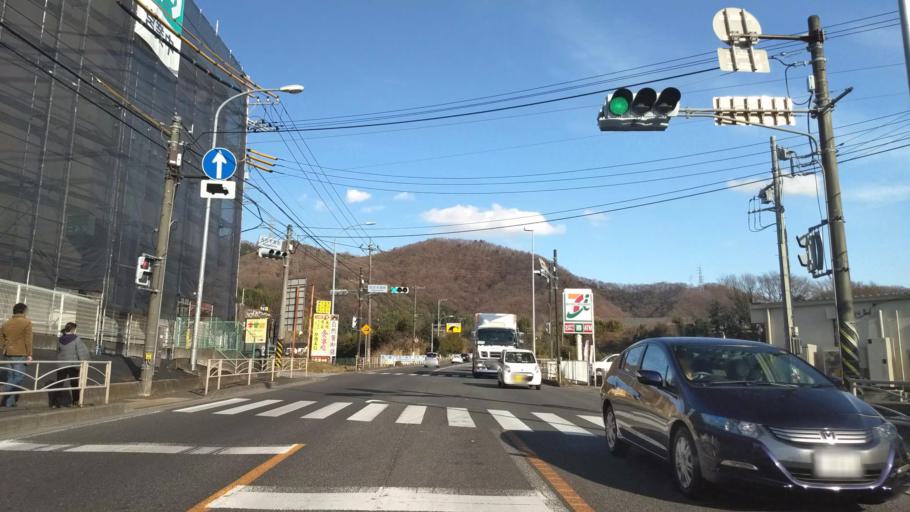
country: JP
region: Kanagawa
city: Hadano
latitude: 35.3828
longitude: 139.2416
